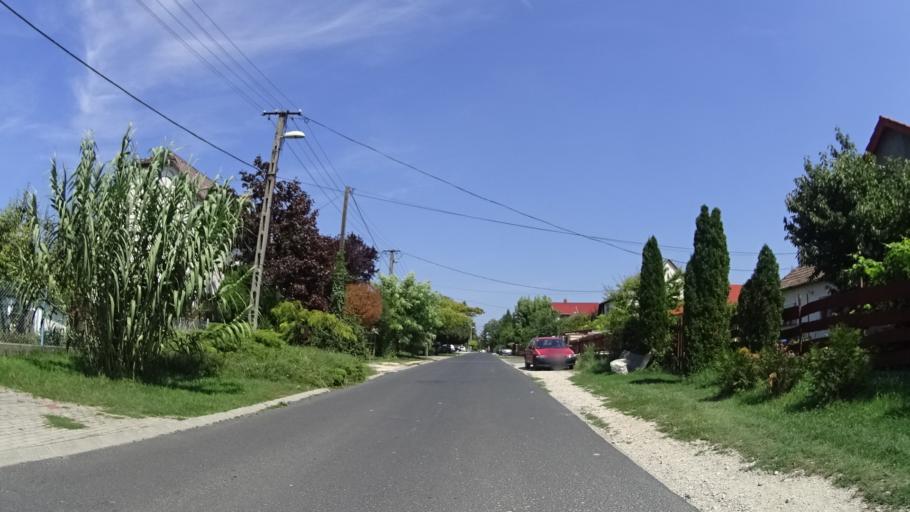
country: HU
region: Fejer
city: Szekesfehervar
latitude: 47.1898
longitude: 18.4521
